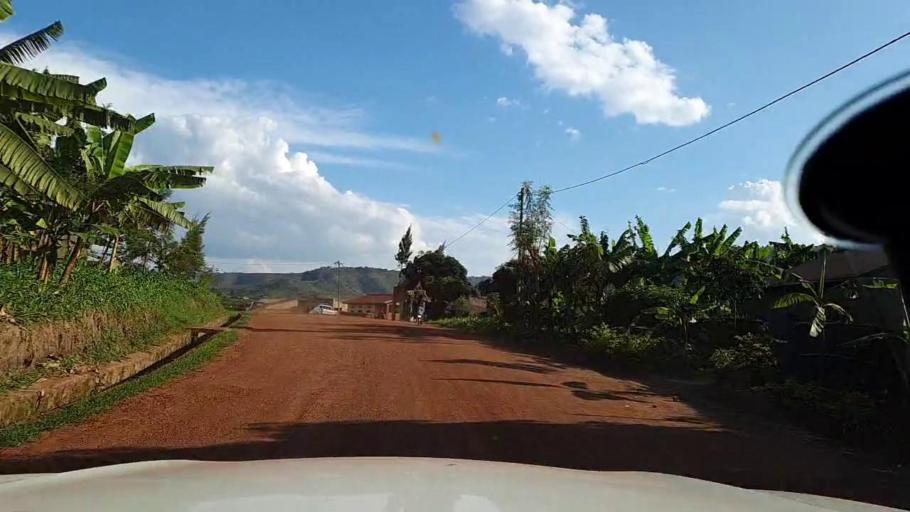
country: RW
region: Kigali
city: Kigali
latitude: -1.8636
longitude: 29.9202
